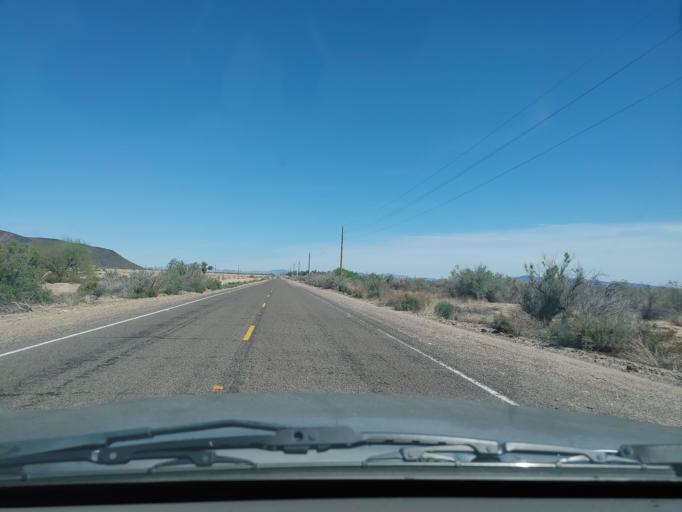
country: US
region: Arizona
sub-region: Maricopa County
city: Gila Bend
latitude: 32.9745
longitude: -113.3060
